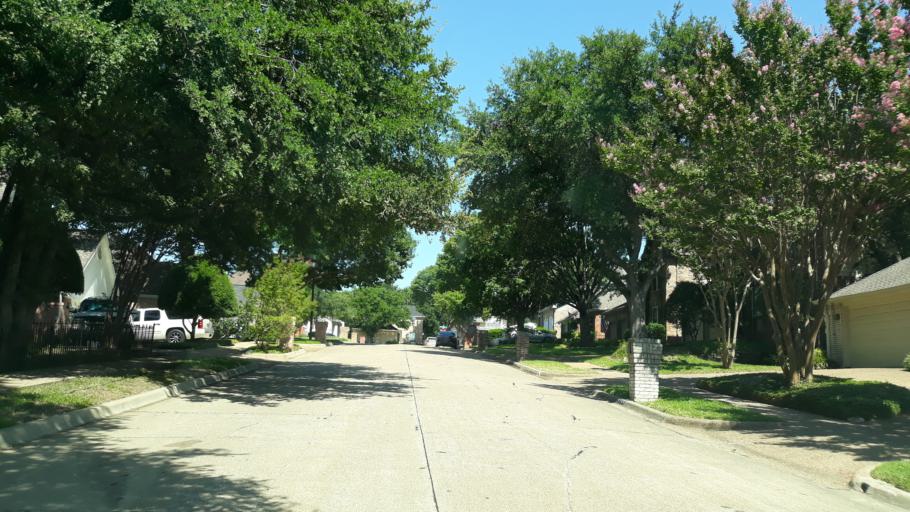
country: US
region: Texas
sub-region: Dallas County
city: Irving
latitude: 32.8205
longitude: -97.0076
